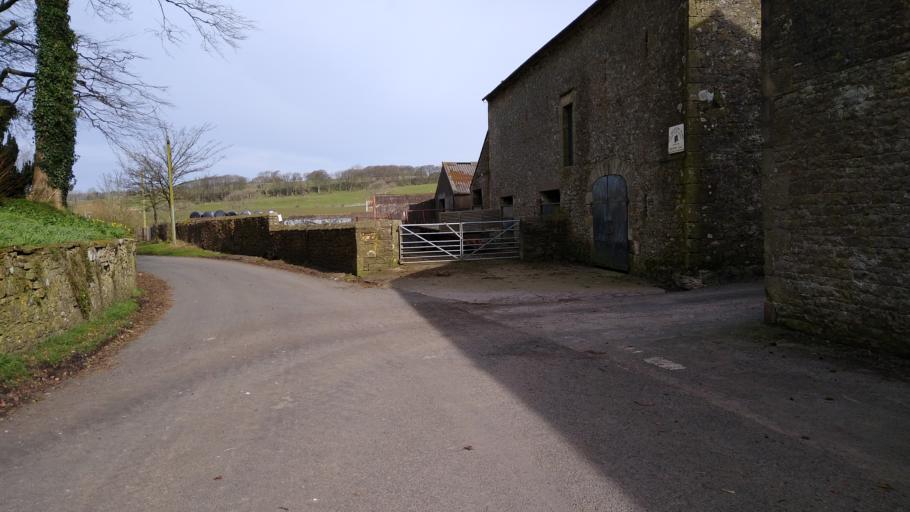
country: GB
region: England
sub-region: Cumbria
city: Cockermouth
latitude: 54.6906
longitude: -3.3705
